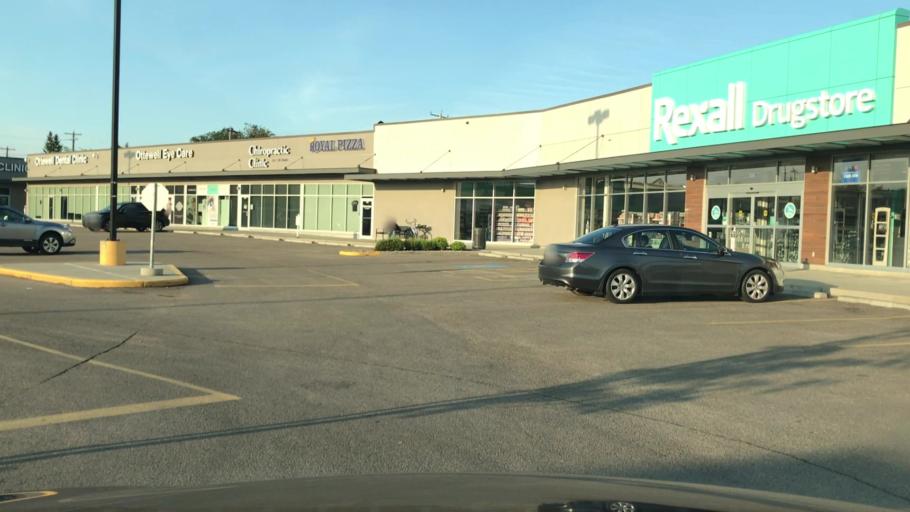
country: CA
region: Alberta
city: Edmonton
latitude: 53.5248
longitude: -113.4273
